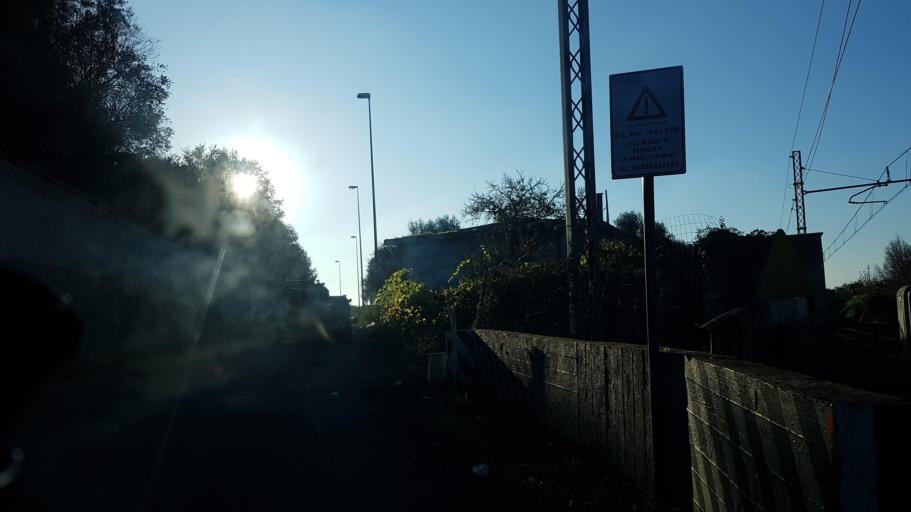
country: IT
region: Apulia
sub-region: Provincia di Brindisi
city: Latiano
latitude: 40.5590
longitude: 17.7349
